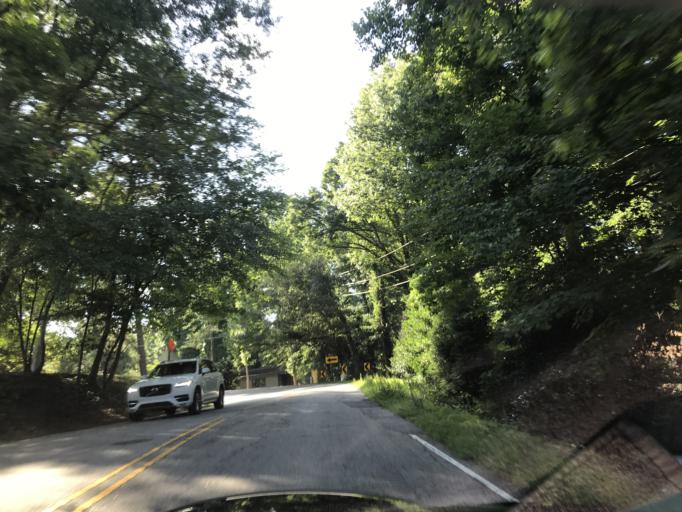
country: US
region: North Carolina
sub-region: Wake County
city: West Raleigh
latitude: 35.8161
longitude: -78.6694
